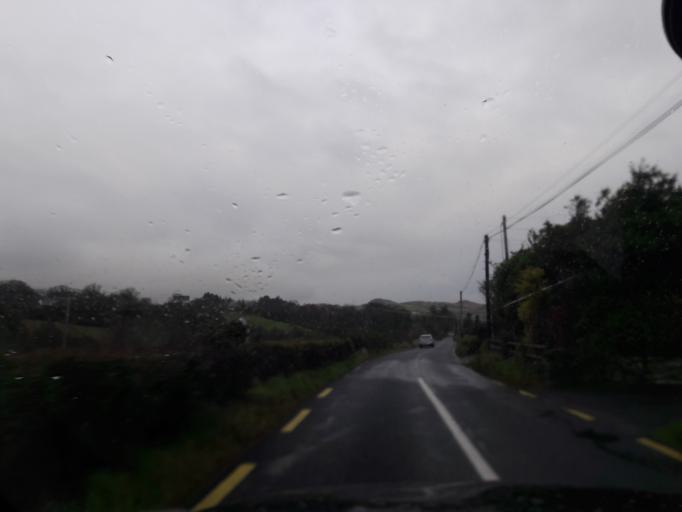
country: IE
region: Ulster
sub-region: County Donegal
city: Ramelton
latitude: 55.2007
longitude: -7.6384
